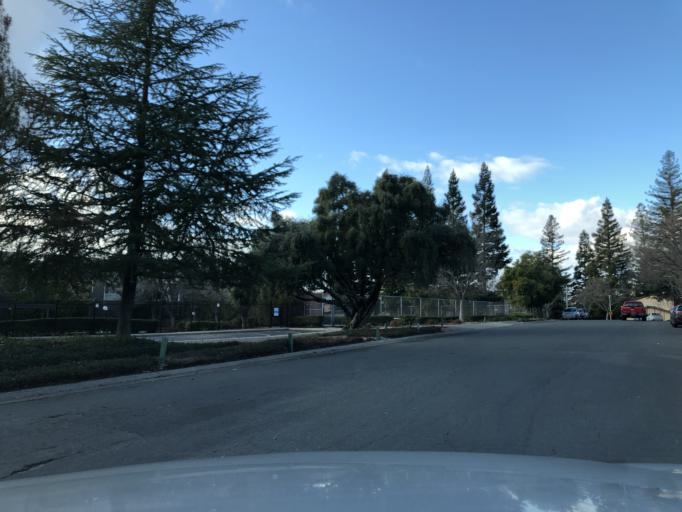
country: US
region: California
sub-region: Sacramento County
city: Foothill Farms
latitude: 38.6558
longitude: -121.3297
